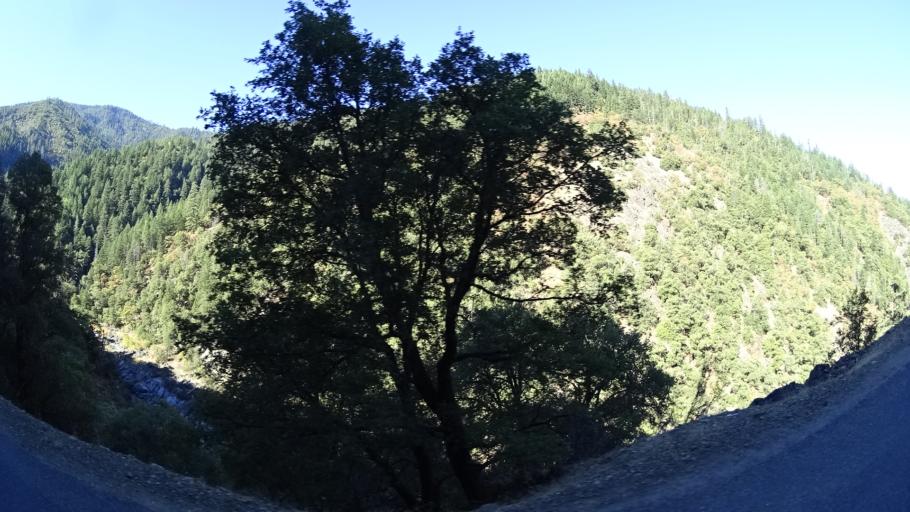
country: US
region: California
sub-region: Humboldt County
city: Willow Creek
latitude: 41.1784
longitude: -123.2191
